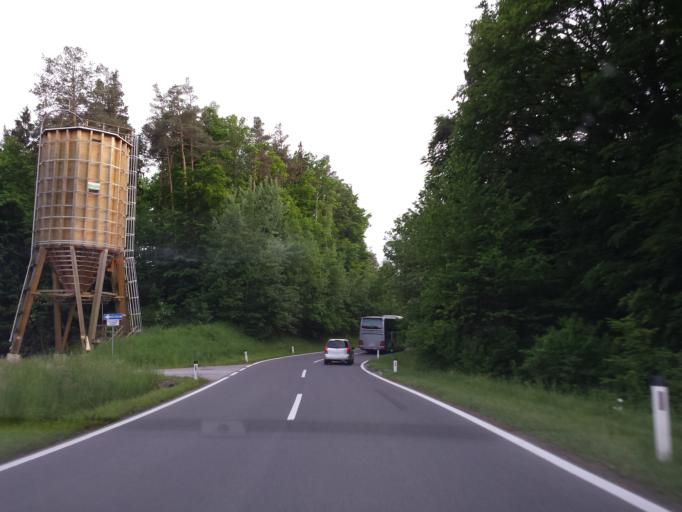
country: AT
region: Styria
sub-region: Graz Stadt
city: Mariatrost
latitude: 47.1008
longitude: 15.5353
